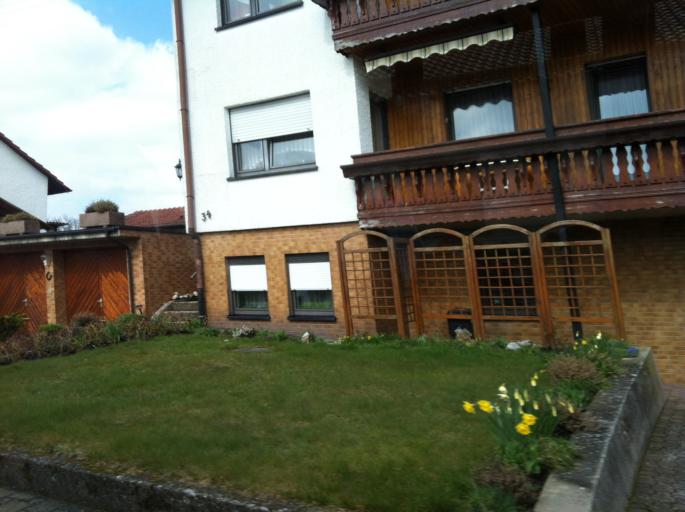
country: DE
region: Baden-Wuerttemberg
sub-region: Karlsruhe Region
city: Fahrenbach
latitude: 49.4133
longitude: 9.1650
